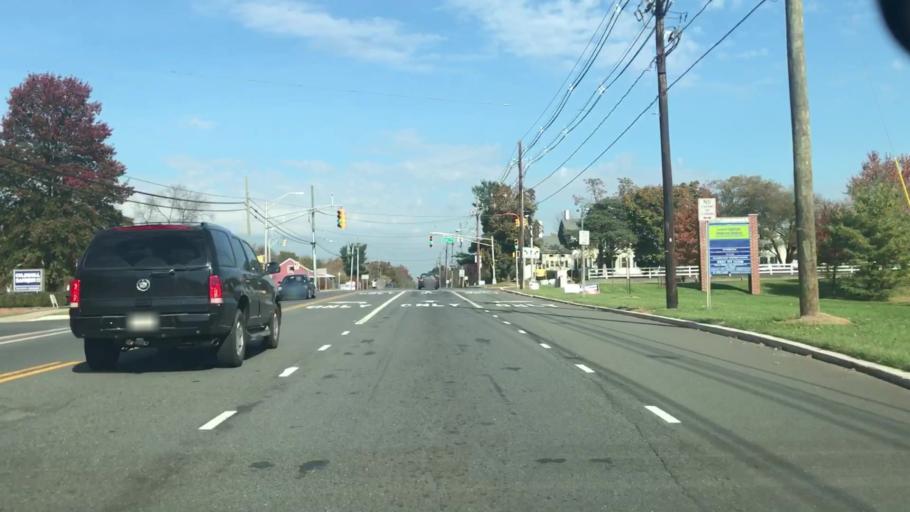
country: US
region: New Jersey
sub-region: Somerset County
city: Bloomingdale
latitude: 40.4934
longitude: -74.6487
